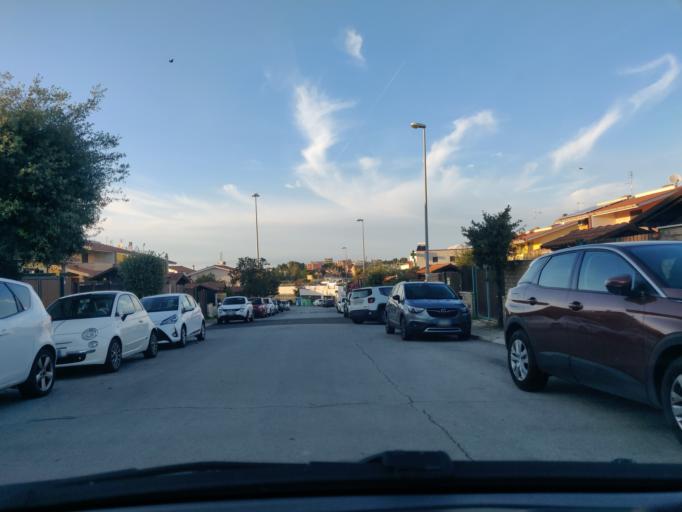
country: IT
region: Latium
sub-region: Citta metropolitana di Roma Capitale
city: Civitavecchia
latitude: 42.0647
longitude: 11.8200
